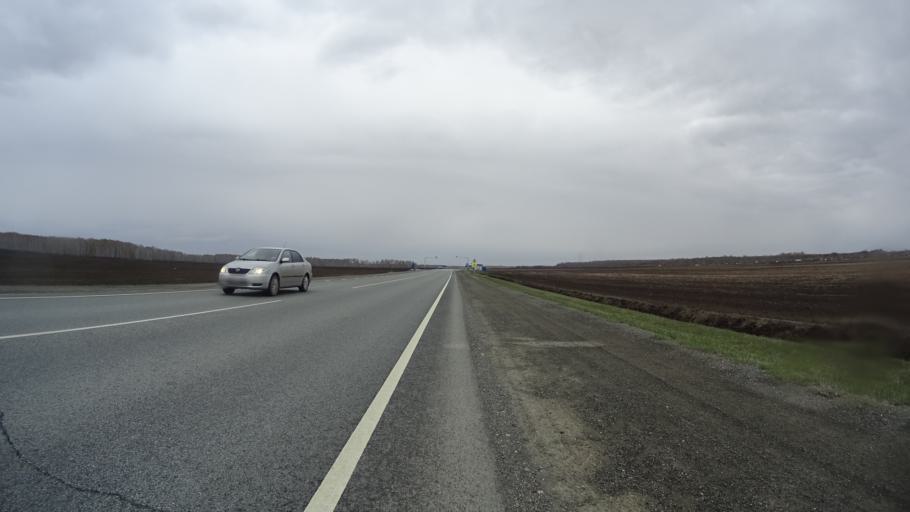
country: RU
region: Chelyabinsk
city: Krasnogorskiy
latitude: 54.5837
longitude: 61.2910
